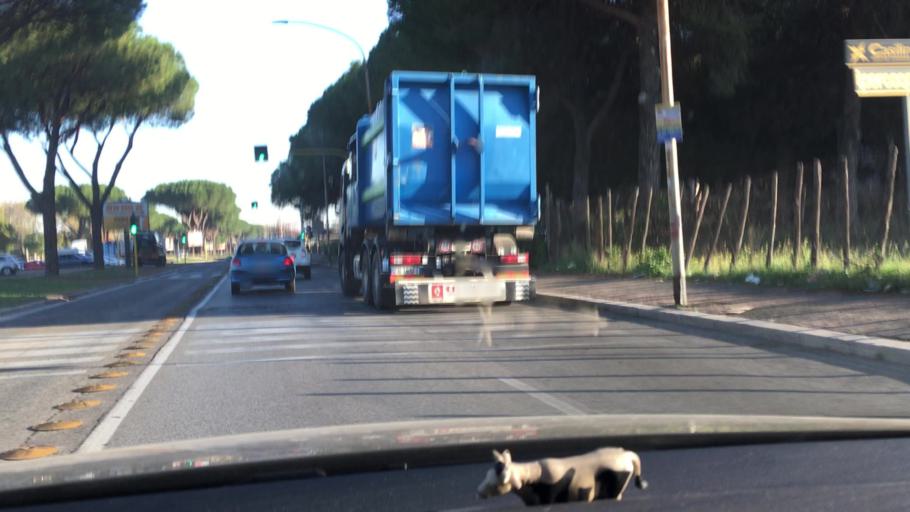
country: IT
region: Latium
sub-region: Citta metropolitana di Roma Capitale
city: Rome
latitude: 41.8686
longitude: 12.5681
